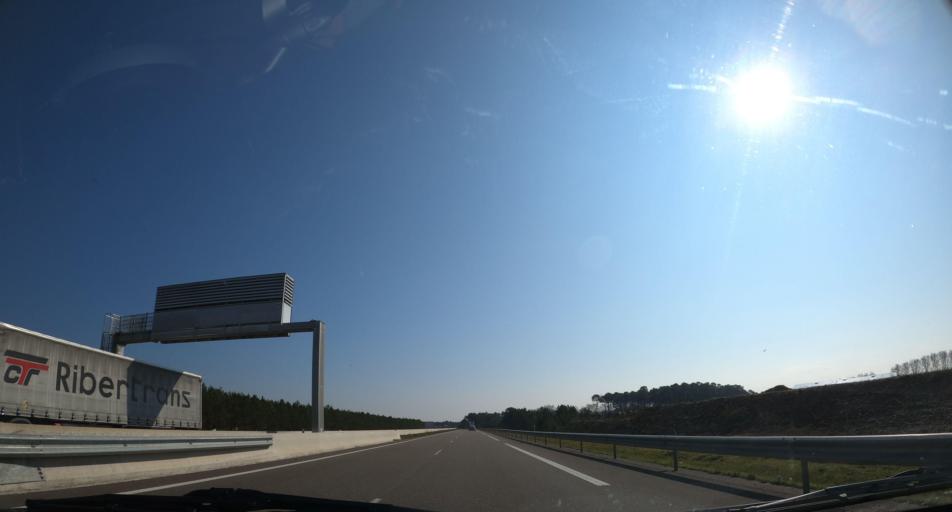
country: FR
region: Aquitaine
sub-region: Departement des Landes
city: Saint-Geours-de-Maremne
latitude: 43.6955
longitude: -1.2181
